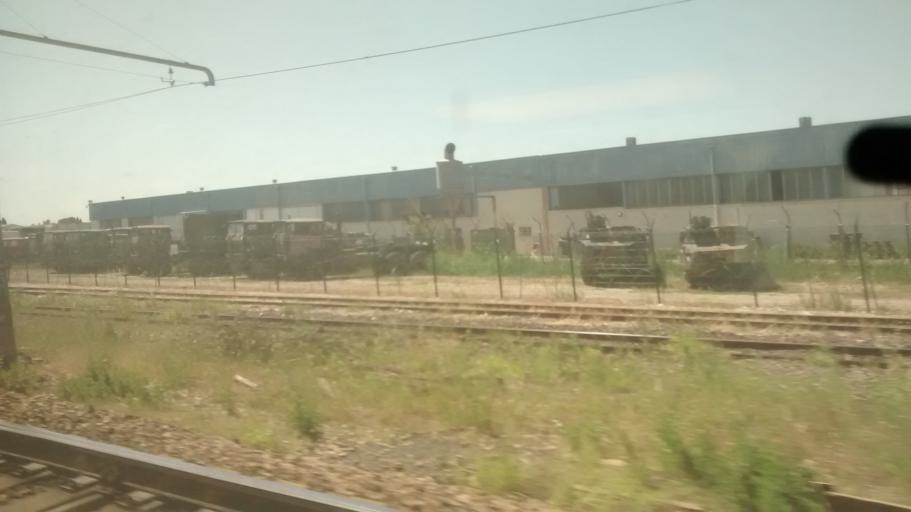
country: FR
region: Languedoc-Roussillon
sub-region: Departement du Gard
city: Milhaud
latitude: 43.8096
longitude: 4.3224
